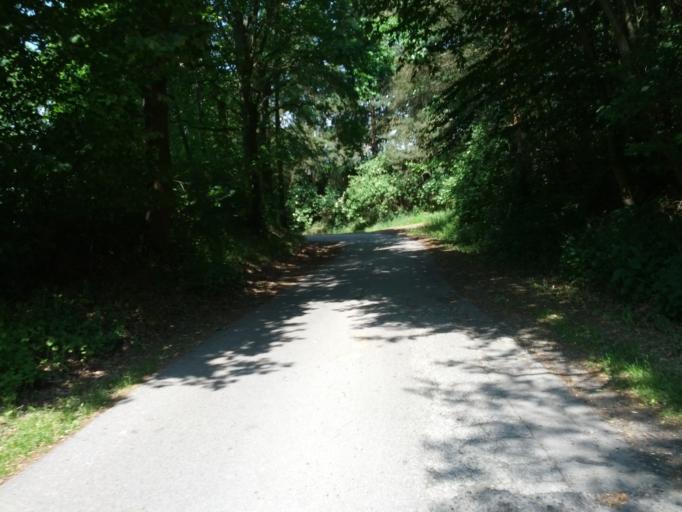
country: DE
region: Thuringia
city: Weilar
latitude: 50.7543
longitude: 10.1584
